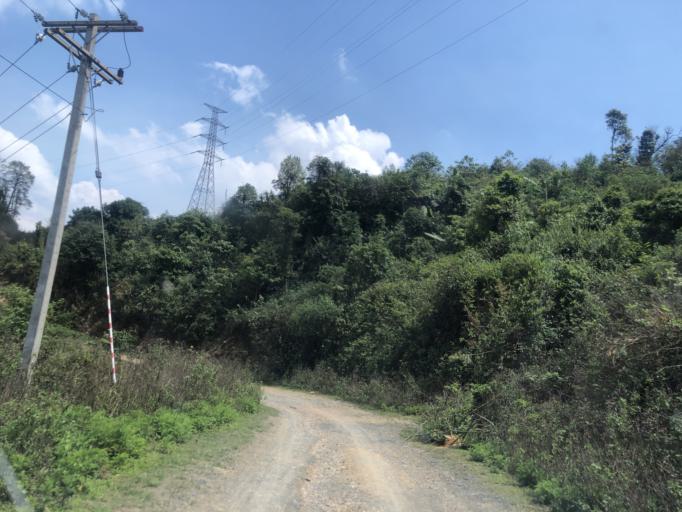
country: LA
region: Phongsali
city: Phongsali
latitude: 21.3899
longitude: 102.1935
